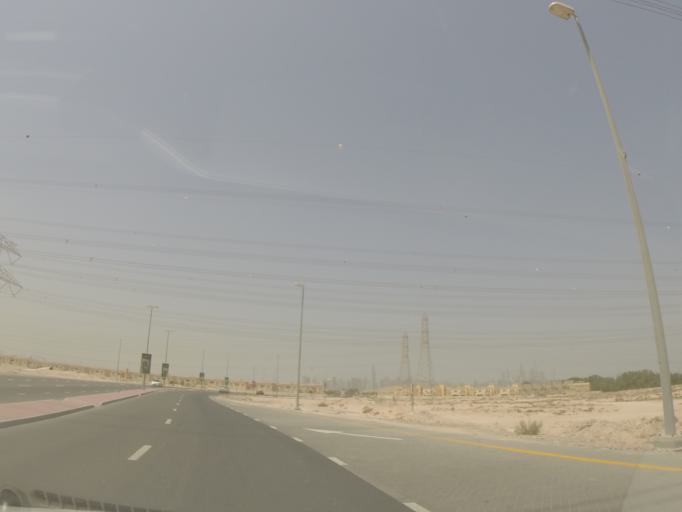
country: AE
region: Dubai
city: Dubai
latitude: 25.0393
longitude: 55.1729
